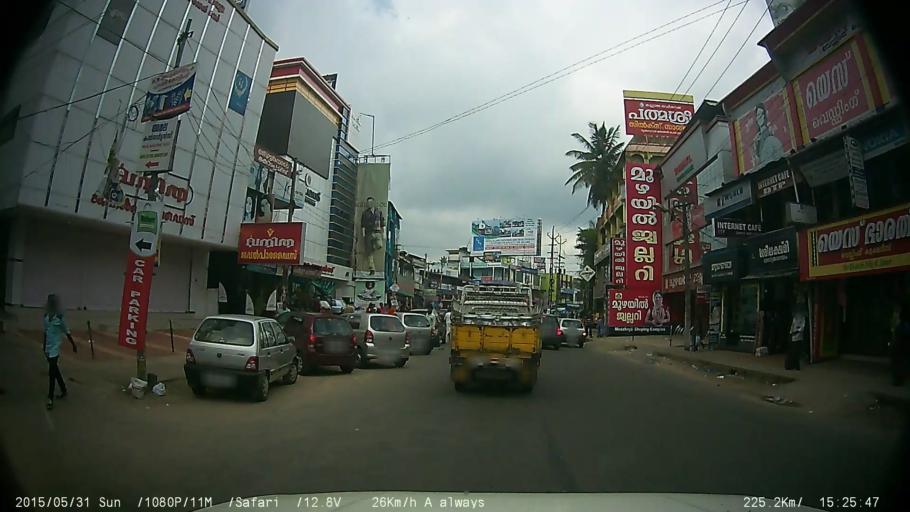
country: IN
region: Kerala
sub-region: Wayanad
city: Panamaram
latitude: 11.6627
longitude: 76.2545
